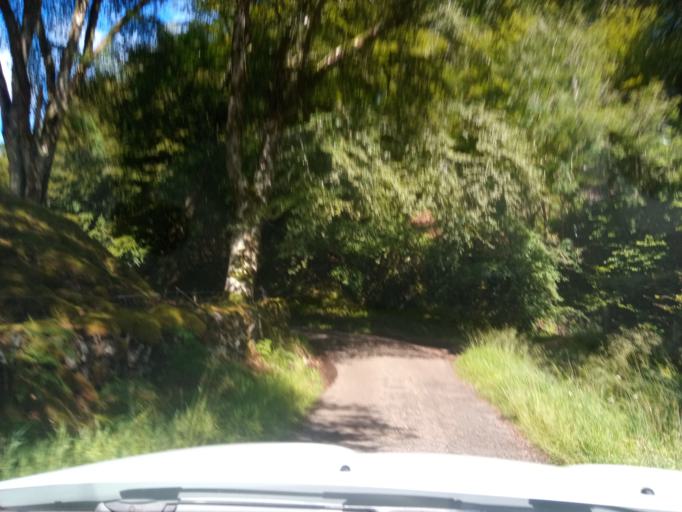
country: GB
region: Scotland
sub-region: Argyll and Bute
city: Isle Of Mull
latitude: 56.7575
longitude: -5.8084
